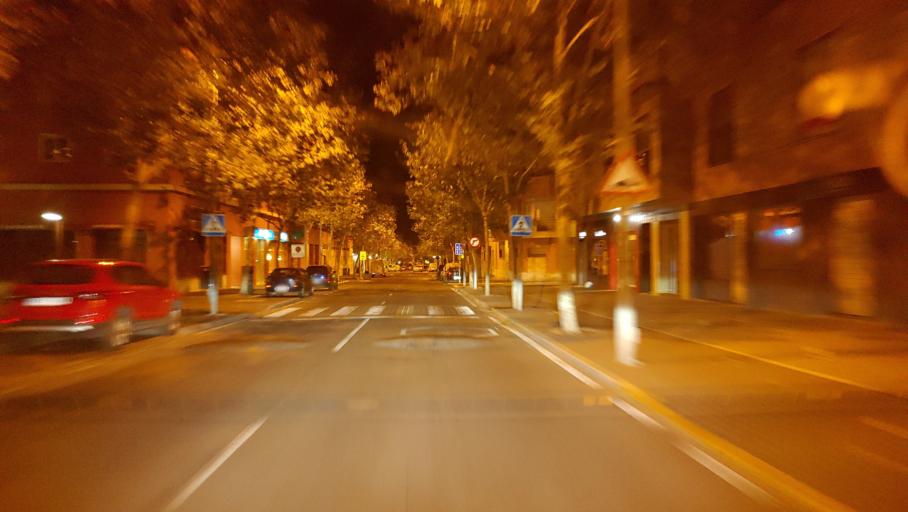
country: ES
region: Castille-La Mancha
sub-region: Provincia de Ciudad Real
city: Ciudad Real
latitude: 38.9786
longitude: -3.9269
